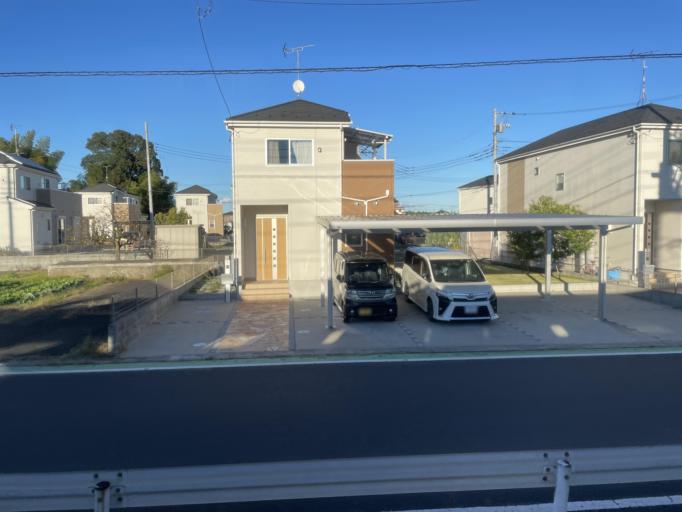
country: JP
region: Saitama
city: Kurihashi
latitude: 36.1079
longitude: 139.7186
